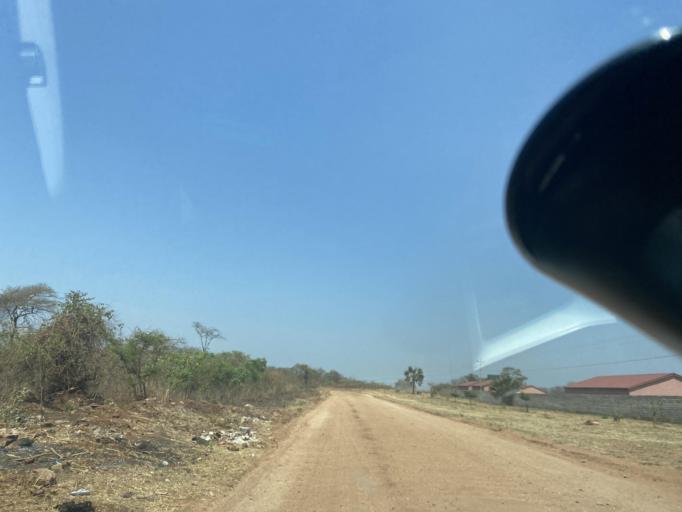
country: ZM
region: Lusaka
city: Lusaka
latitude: -15.5231
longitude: 28.1096
